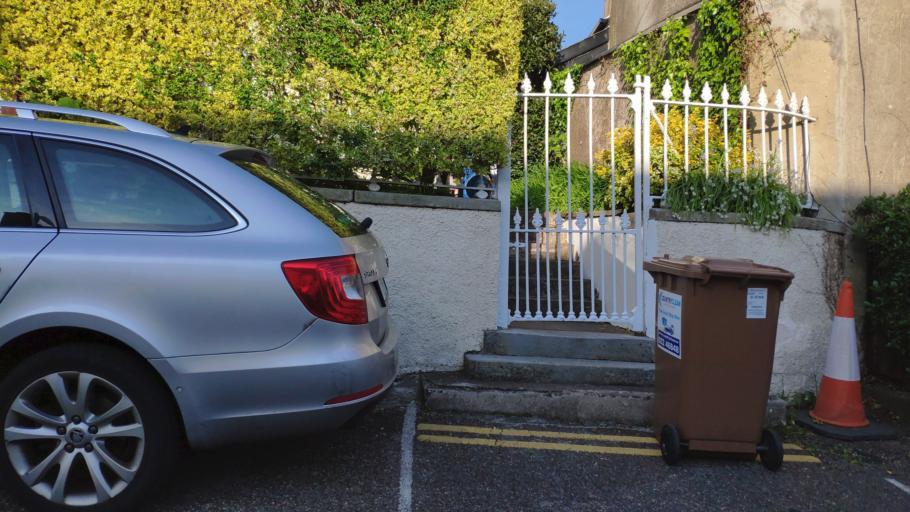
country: IE
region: Munster
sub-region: County Cork
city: Cork
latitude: 51.9043
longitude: -8.4698
